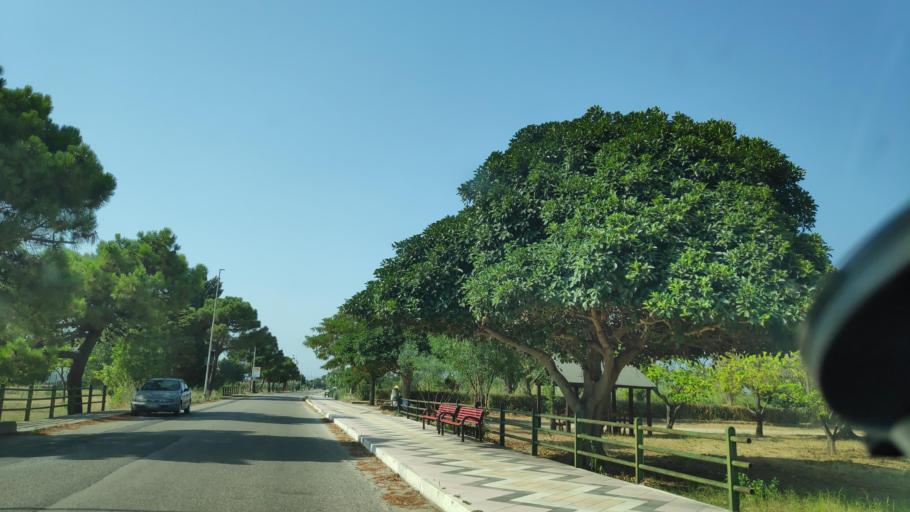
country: IT
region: Calabria
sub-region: Provincia di Catanzaro
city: Badolato Marina
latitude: 38.5726
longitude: 16.5690
